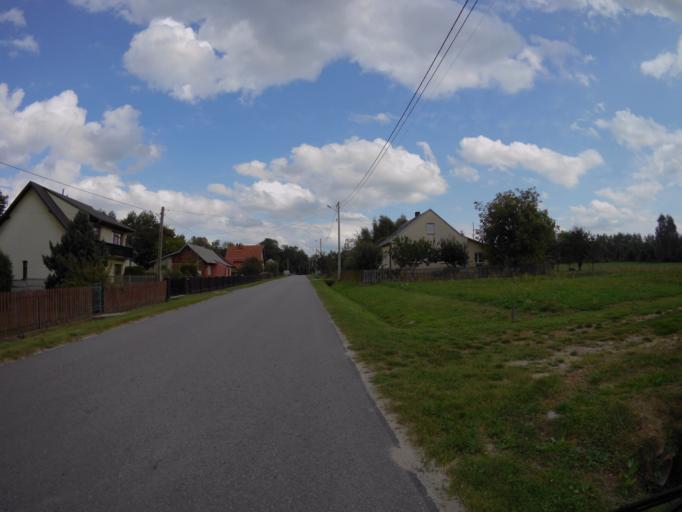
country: PL
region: Subcarpathian Voivodeship
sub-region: Powiat lezajski
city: Brzoza Krolewska
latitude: 50.2439
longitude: 22.3340
